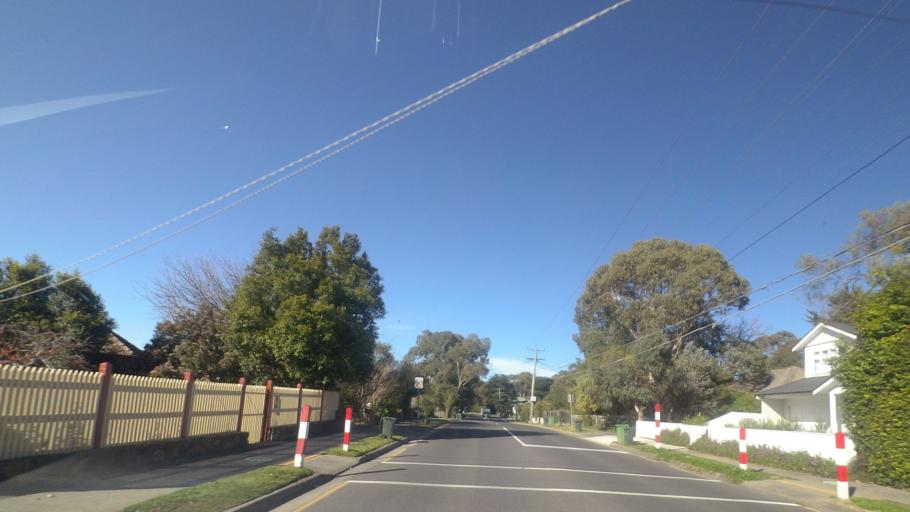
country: AU
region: Victoria
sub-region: Banyule
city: Montmorency
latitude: -37.7183
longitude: 145.1236
